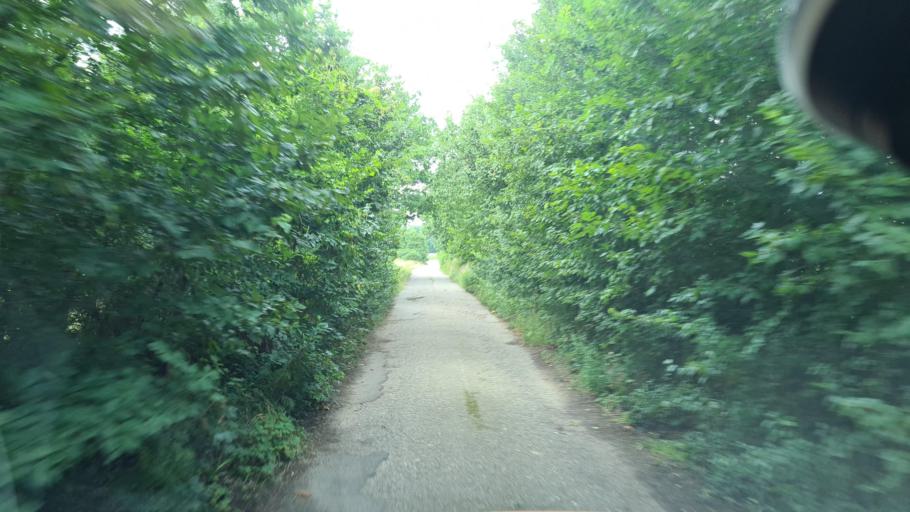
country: DE
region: Brandenburg
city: Drebkau
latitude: 51.6356
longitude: 14.2906
